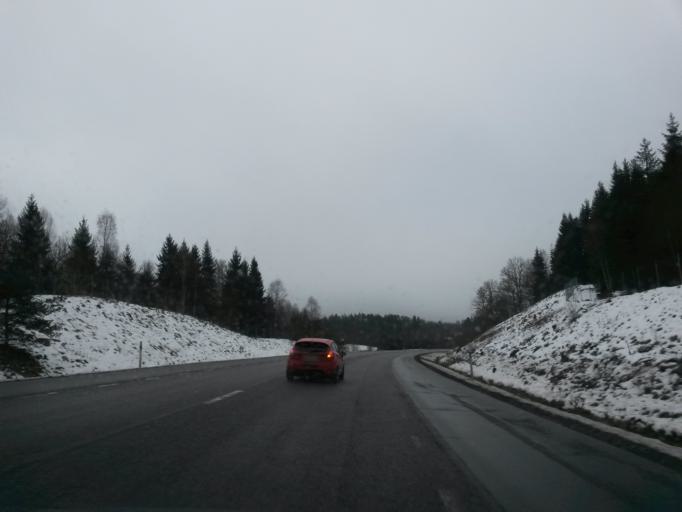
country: SE
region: Vaestra Goetaland
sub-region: Boras Kommun
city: Viskafors
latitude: 57.6037
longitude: 12.8738
